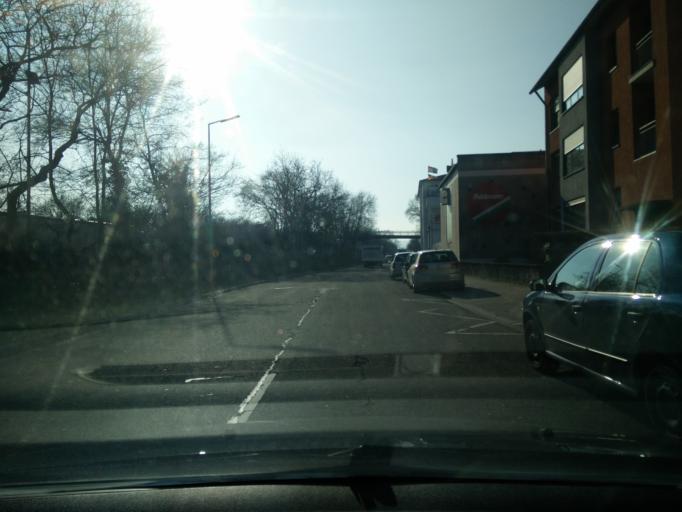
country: DE
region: Baden-Wuerttemberg
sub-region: Karlsruhe Region
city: Karlsruhe
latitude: 49.0005
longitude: 8.3686
